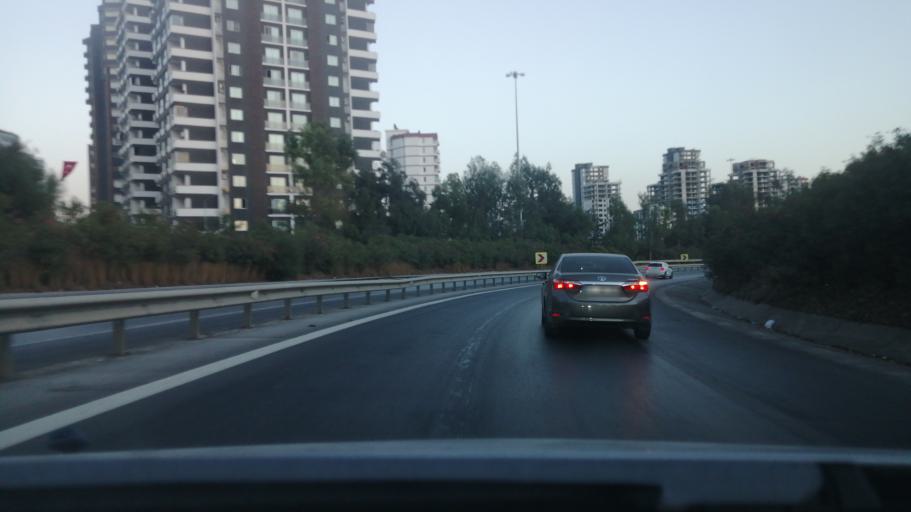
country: TR
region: Adana
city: Seyhan
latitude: 37.0343
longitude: 35.2523
